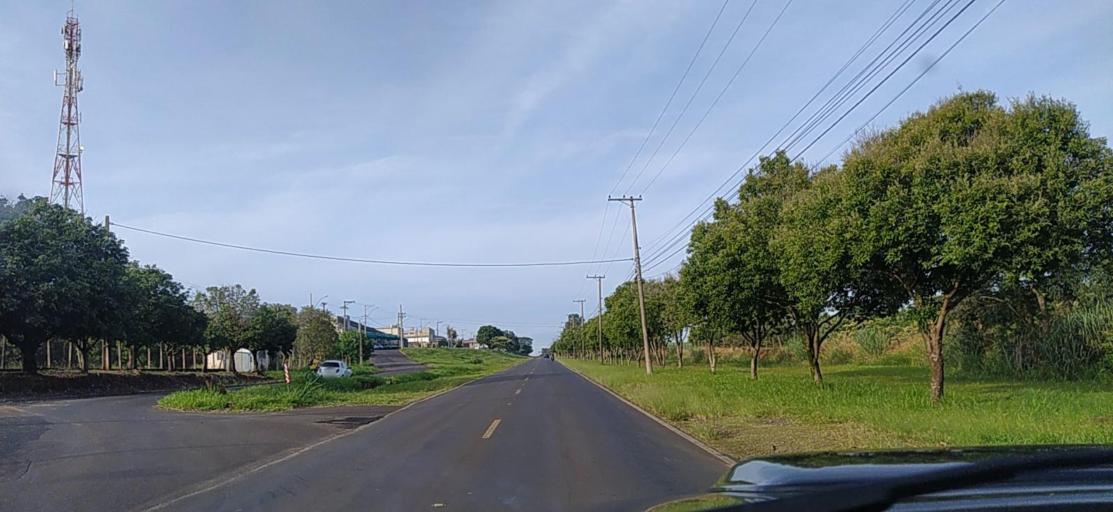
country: BR
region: Sao Paulo
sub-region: Pindorama
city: Pindorama
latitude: -21.1946
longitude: -48.9169
